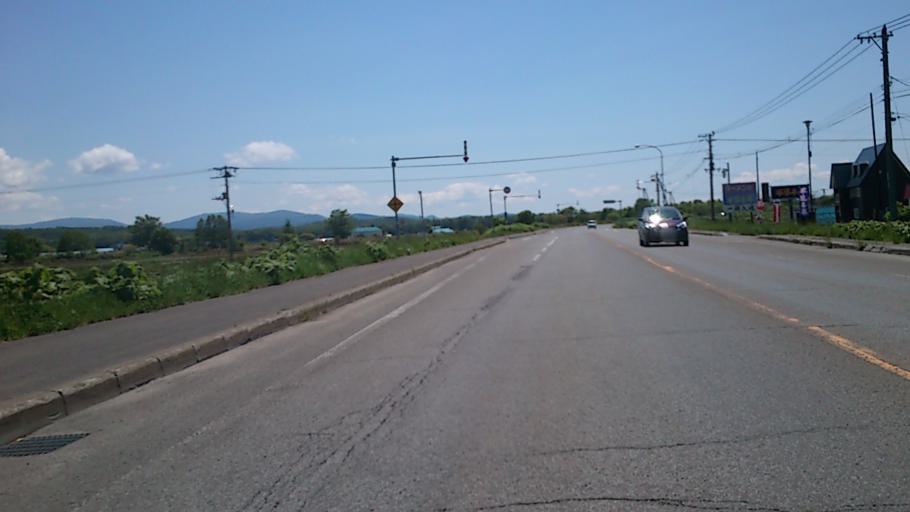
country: JP
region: Hokkaido
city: Nayoro
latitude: 44.3179
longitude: 142.4572
